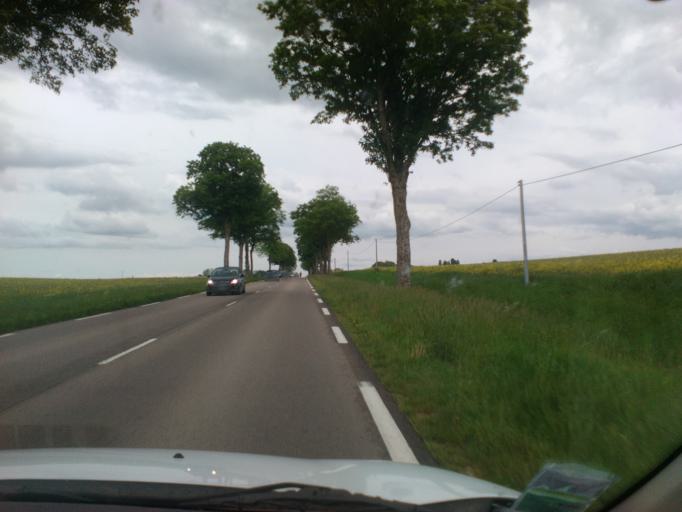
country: FR
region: Champagne-Ardenne
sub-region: Departement de l'Aube
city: Vendeuvre-sur-Barse
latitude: 48.2375
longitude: 4.5241
